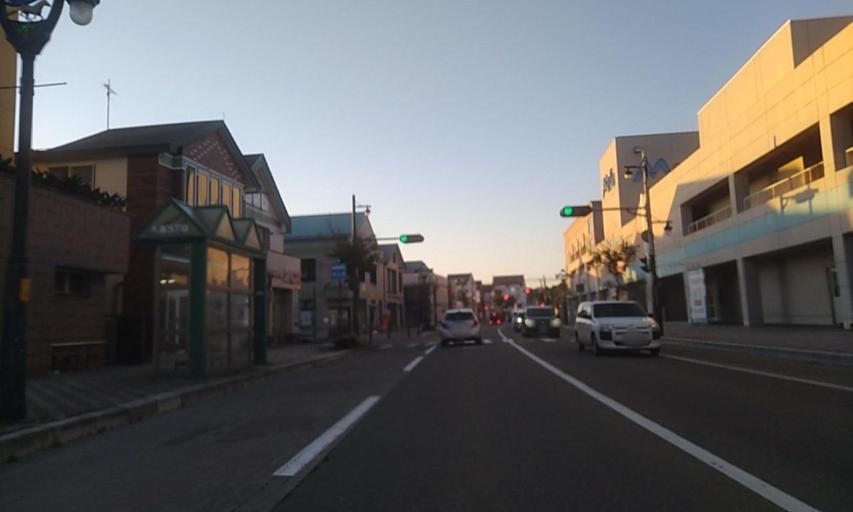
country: JP
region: Hokkaido
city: Shizunai-furukawacho
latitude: 42.1614
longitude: 142.7756
